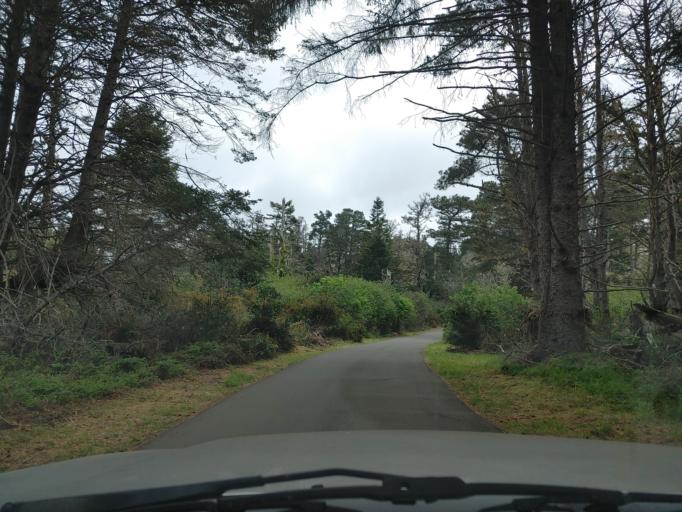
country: US
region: California
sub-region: Mendocino County
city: Fort Bragg
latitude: 39.3294
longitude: -123.8091
